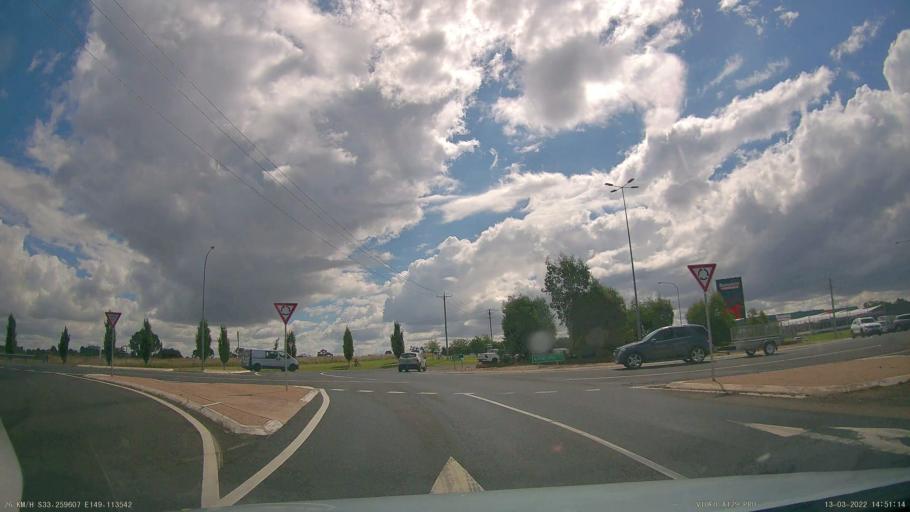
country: AU
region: New South Wales
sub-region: Orange Municipality
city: Orange
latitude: -33.2595
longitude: 149.1135
